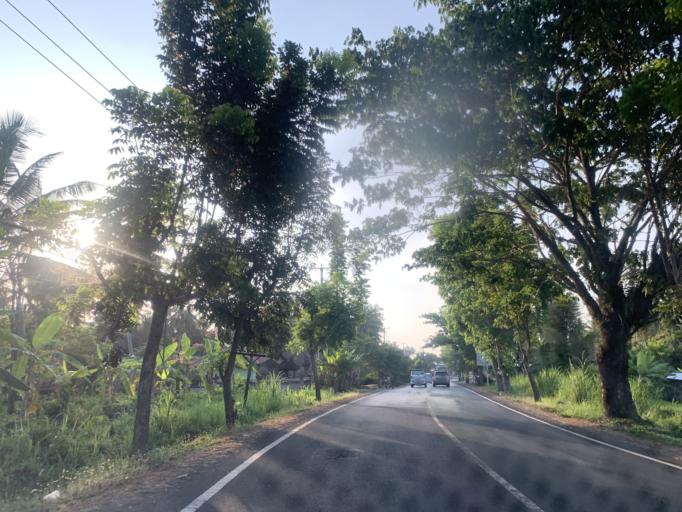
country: ID
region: Bali
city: Banjar Delodrurung
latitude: -8.4925
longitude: 114.9582
